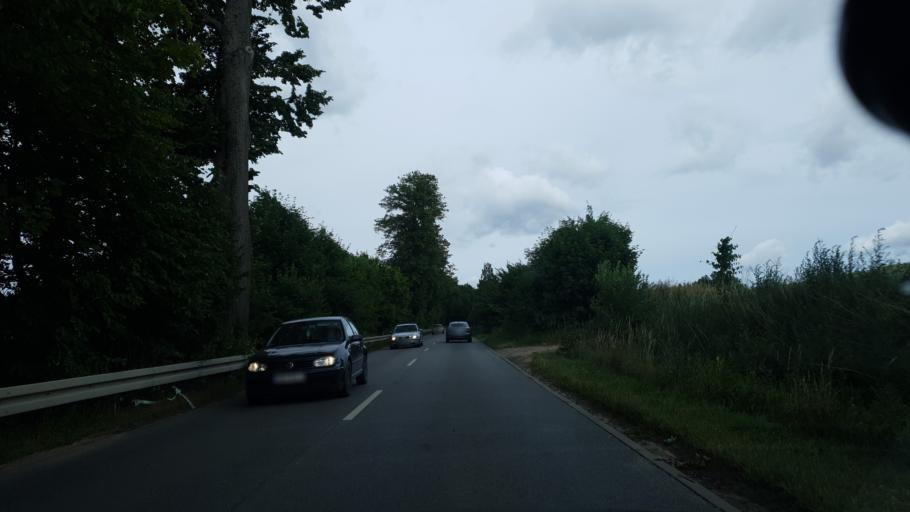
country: PL
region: Pomeranian Voivodeship
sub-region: Powiat kartuski
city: Przodkowo
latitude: 54.3827
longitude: 18.3215
